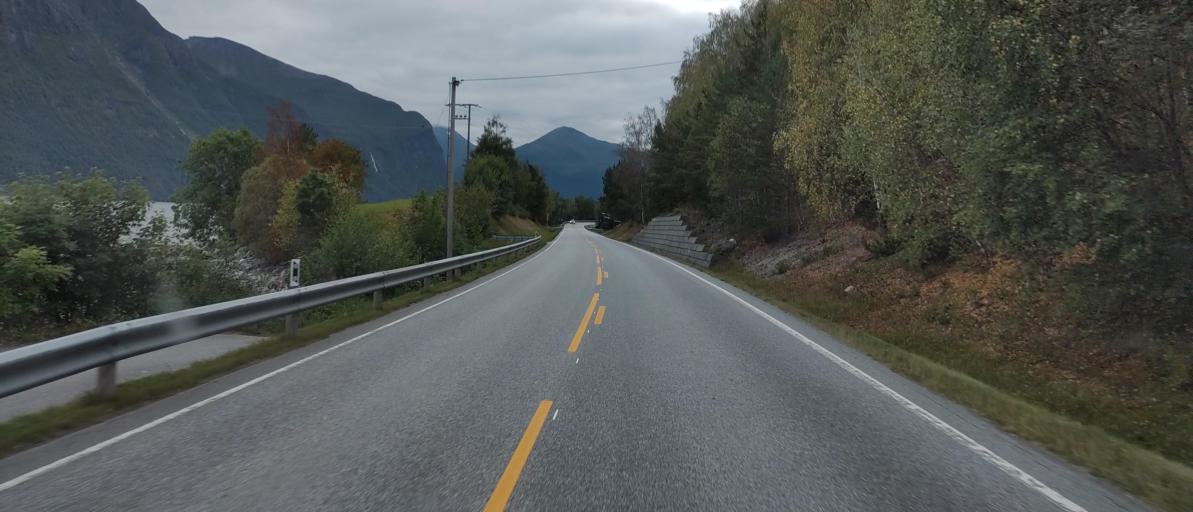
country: NO
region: More og Romsdal
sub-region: Rauma
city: Andalsnes
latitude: 62.5714
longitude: 7.6510
